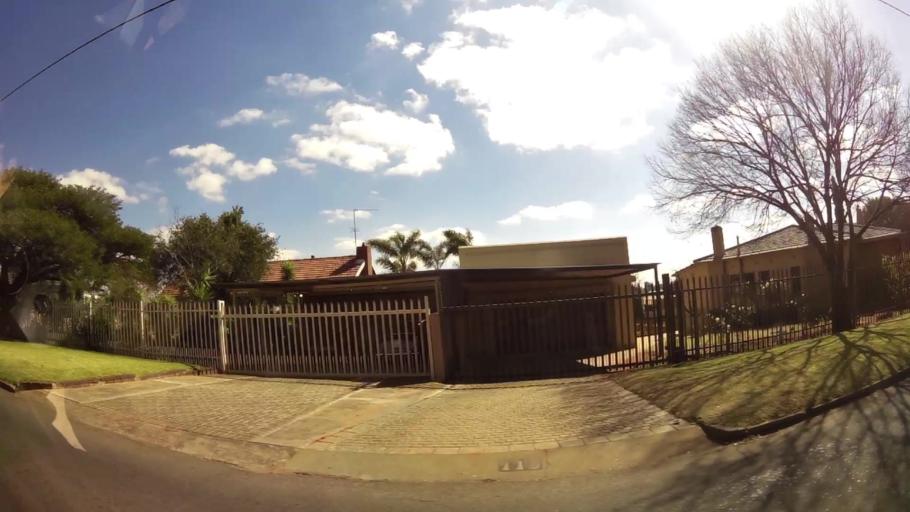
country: ZA
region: Gauteng
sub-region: West Rand District Municipality
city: Krugersdorp
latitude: -26.0927
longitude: 27.7842
